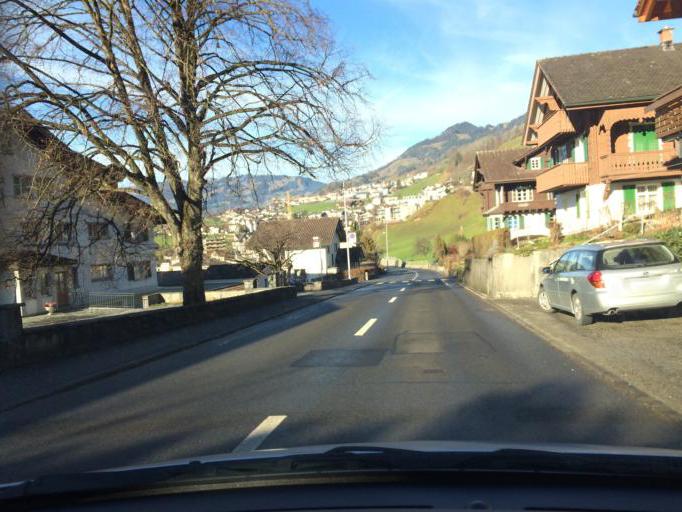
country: CH
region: Schwyz
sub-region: Bezirk Schwyz
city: Schwyz
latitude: 47.0194
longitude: 8.6627
